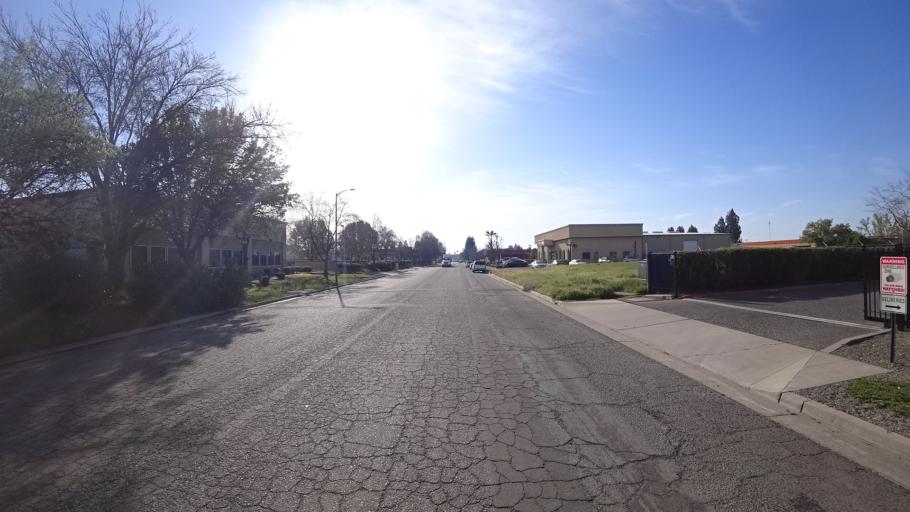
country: US
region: California
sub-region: Fresno County
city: West Park
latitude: 36.8131
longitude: -119.8778
